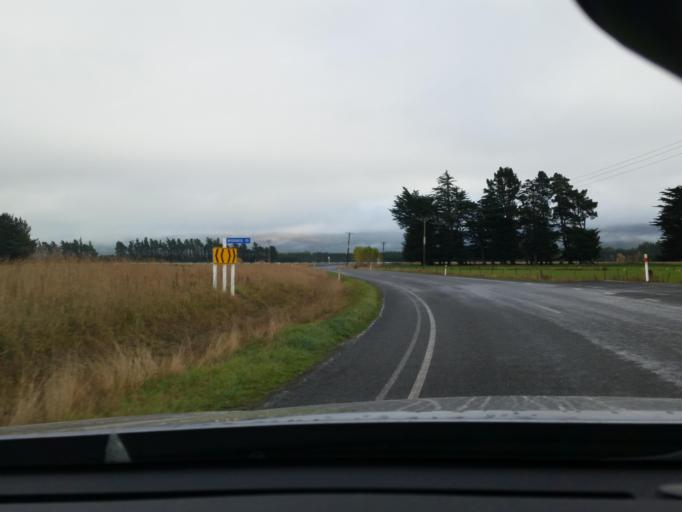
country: NZ
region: Southland
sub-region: Southland District
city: Winton
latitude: -45.8815
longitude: 168.3381
